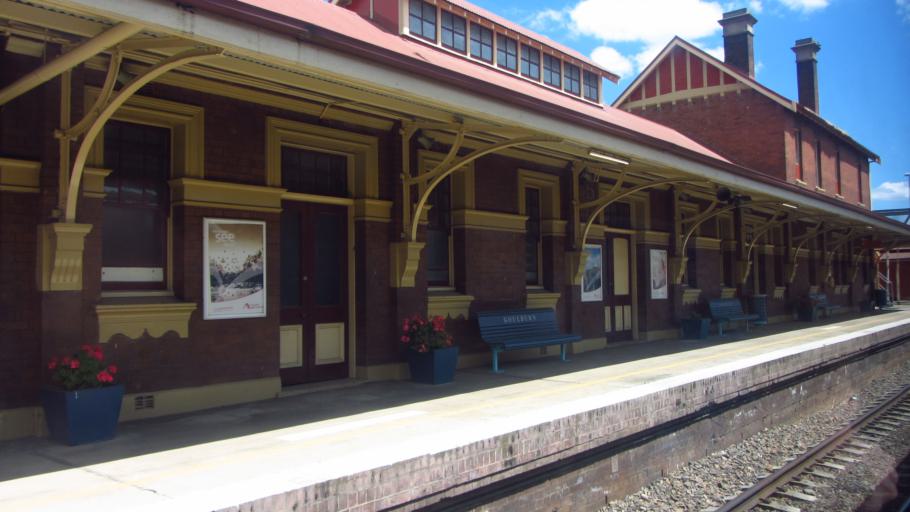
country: AU
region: New South Wales
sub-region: Goulburn Mulwaree
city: Goulburn
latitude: -34.7581
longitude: 149.7195
